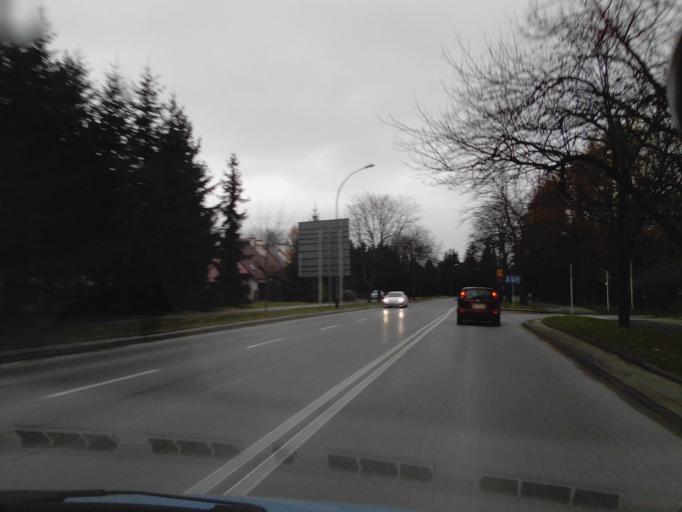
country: PL
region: Subcarpathian Voivodeship
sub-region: Rzeszow
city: Rzeszow
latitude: 50.0208
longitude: 22.0036
